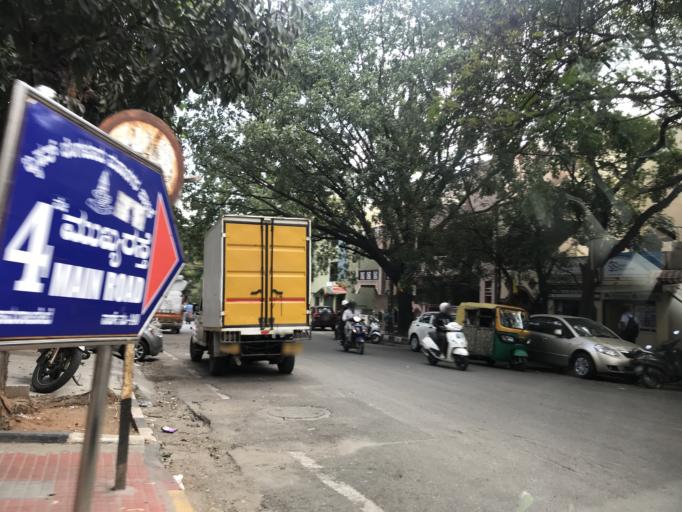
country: IN
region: Karnataka
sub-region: Bangalore Urban
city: Bangalore
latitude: 12.9579
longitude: 77.5621
